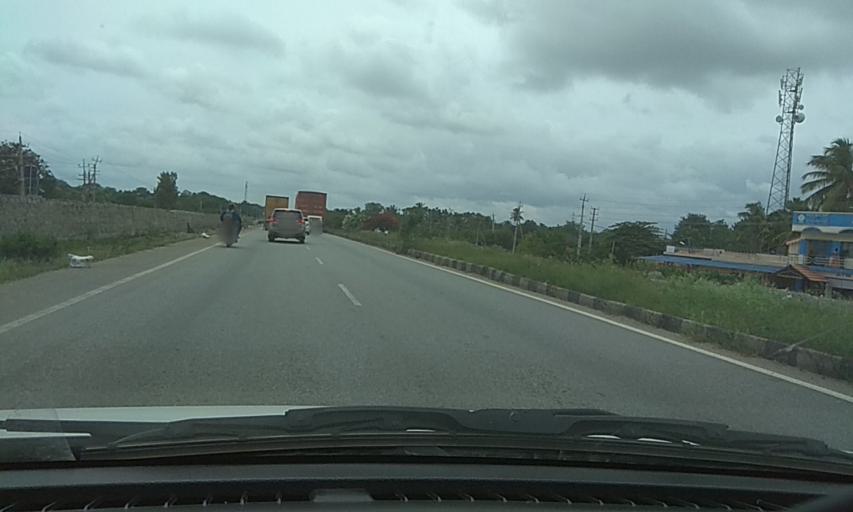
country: IN
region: Karnataka
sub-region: Davanagere
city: Mayakonda
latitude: 14.3169
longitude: 76.2404
